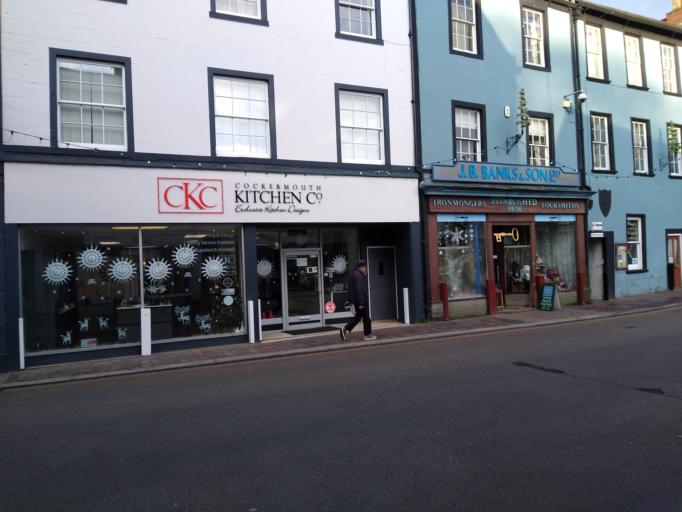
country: GB
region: England
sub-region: Cumbria
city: Cockermouth
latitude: 54.6642
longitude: -3.3616
